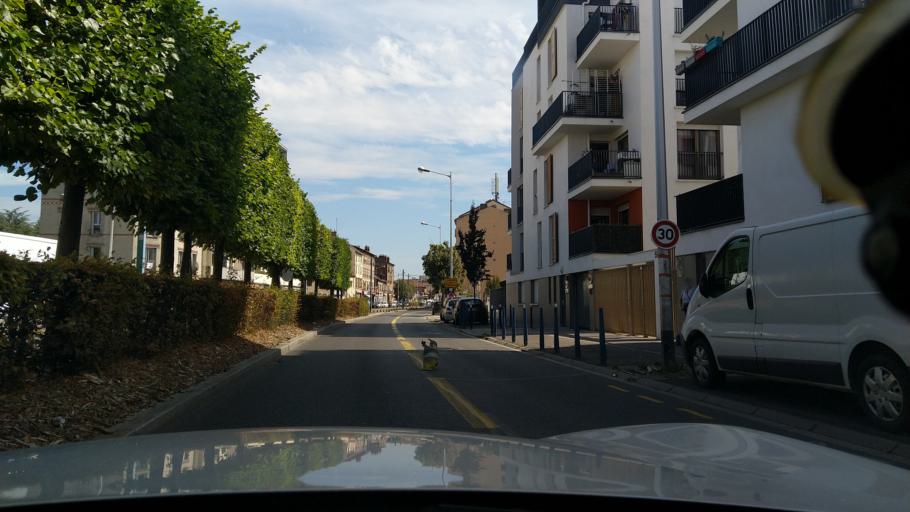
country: FR
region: Ile-de-France
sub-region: Departement de Seine-Saint-Denis
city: La Courneuve
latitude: 48.9238
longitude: 2.4042
